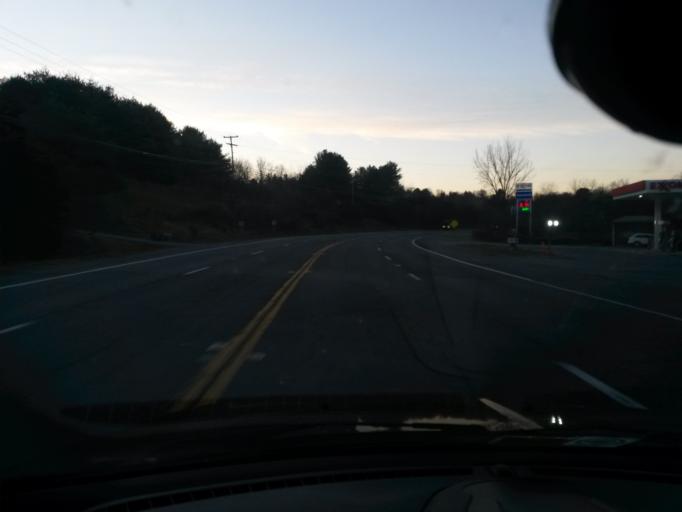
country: US
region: Virginia
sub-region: Botetourt County
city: Fincastle
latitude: 37.5075
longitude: -79.8773
